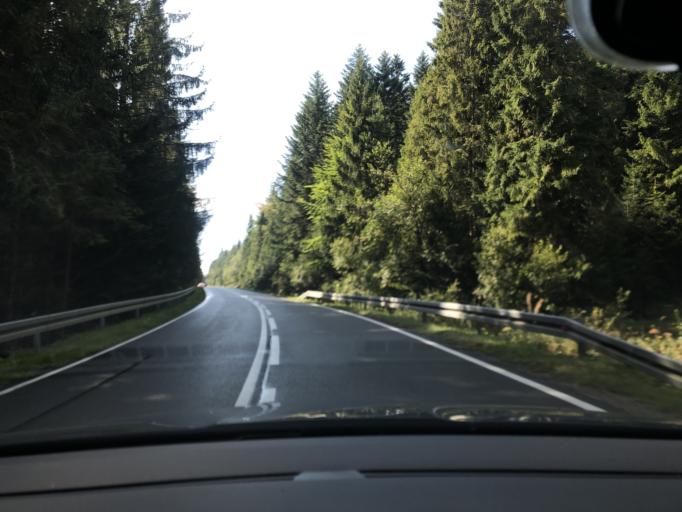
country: PL
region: Lesser Poland Voivodeship
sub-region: Powiat nowotarski
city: Zubrzyca Gorna
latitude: 49.5864
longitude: 19.6075
